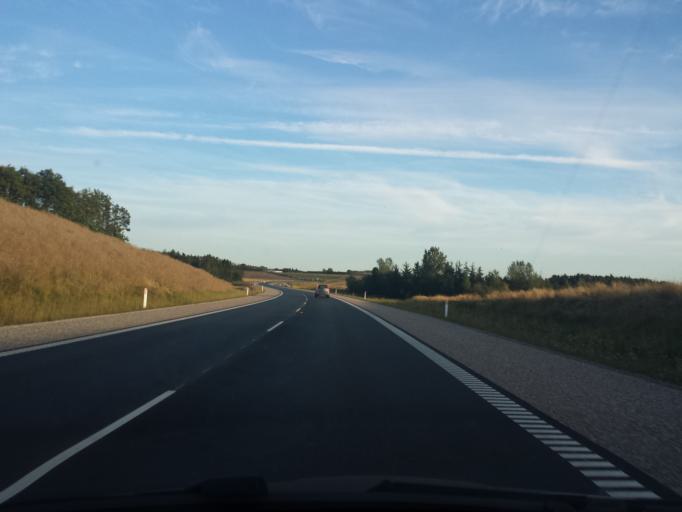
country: DK
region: Capital Region
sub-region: Egedal Kommune
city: Smorumnedre
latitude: 55.7270
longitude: 12.2844
